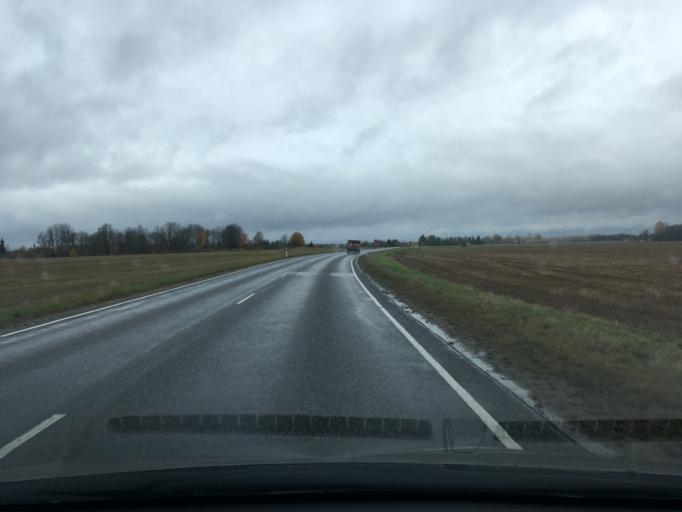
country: EE
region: Jogevamaa
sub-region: Tabivere vald
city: Tabivere
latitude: 58.4632
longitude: 26.6340
